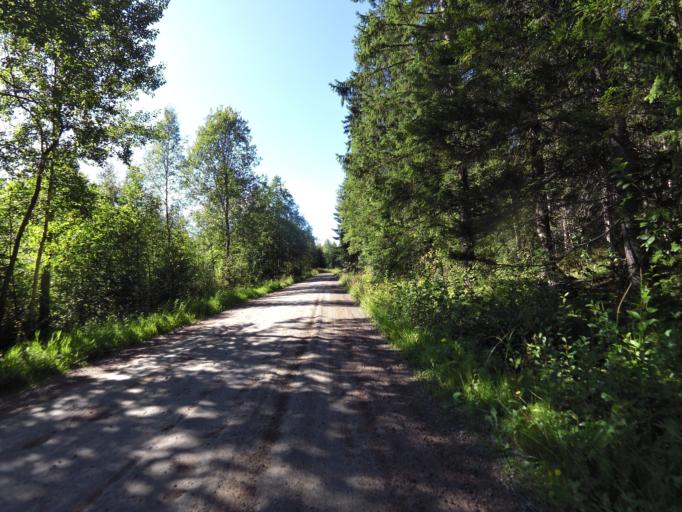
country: SE
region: Gaevleborg
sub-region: Hofors Kommun
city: Hofors
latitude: 60.5419
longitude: 16.4029
